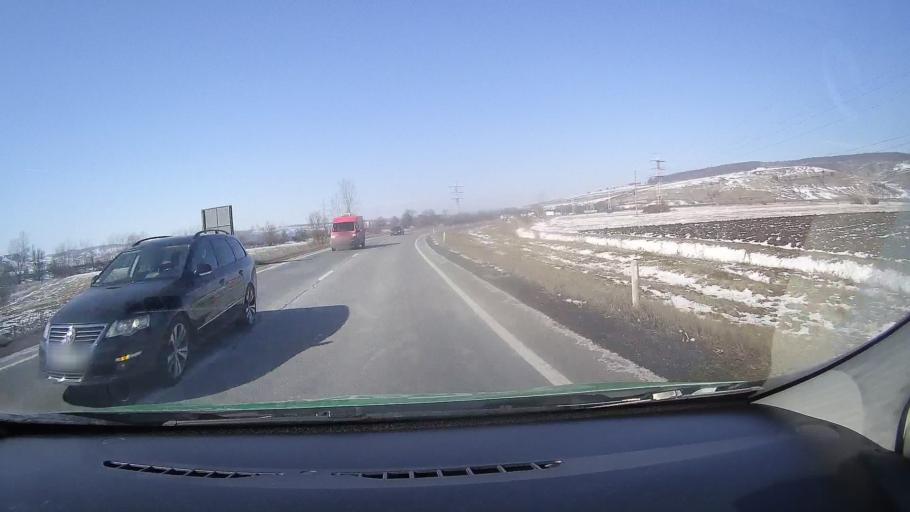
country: RO
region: Brasov
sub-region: Comuna Hoghiz
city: Hoghiz
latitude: 45.9981
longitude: 25.2955
